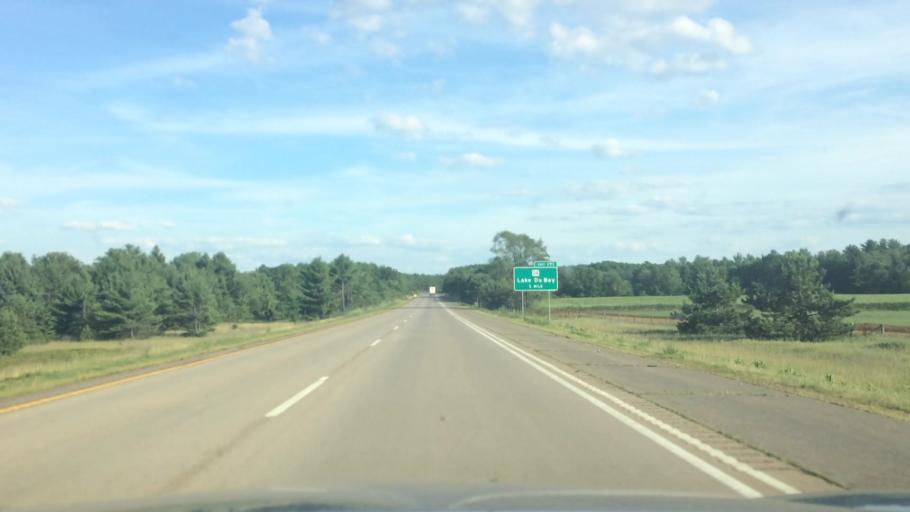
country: US
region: Wisconsin
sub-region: Marathon County
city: Mosinee
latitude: 44.6973
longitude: -89.6483
